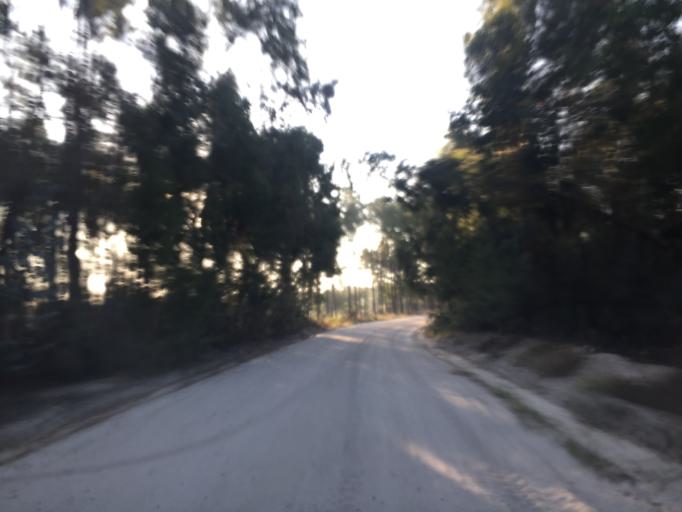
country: PT
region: Portalegre
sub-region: Ponte de Sor
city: Santo Andre
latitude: 39.0924
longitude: -8.3696
